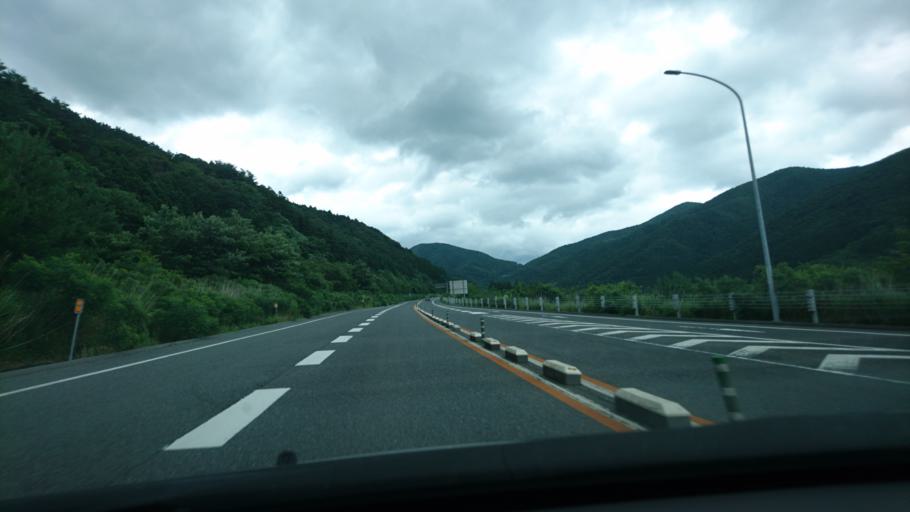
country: JP
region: Iwate
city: Ofunato
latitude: 39.1255
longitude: 141.7400
